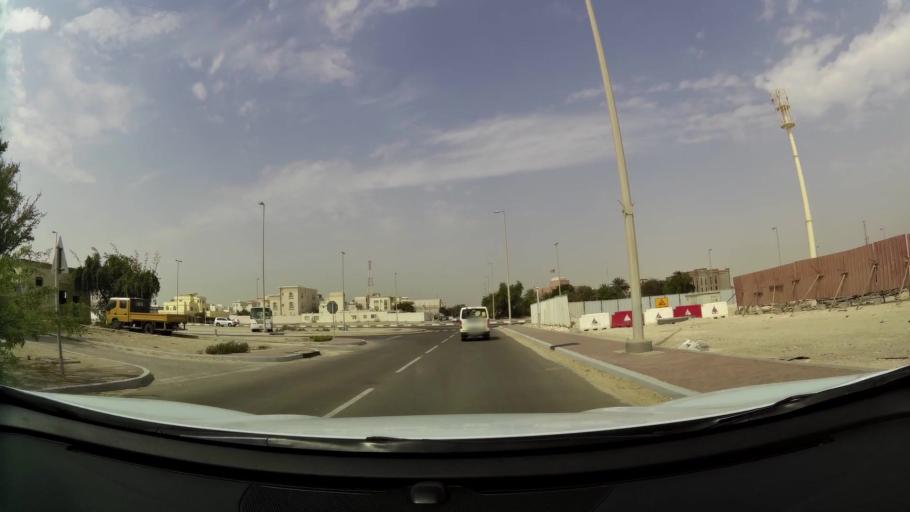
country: AE
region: Abu Dhabi
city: Abu Dhabi
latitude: 24.3095
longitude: 54.6121
